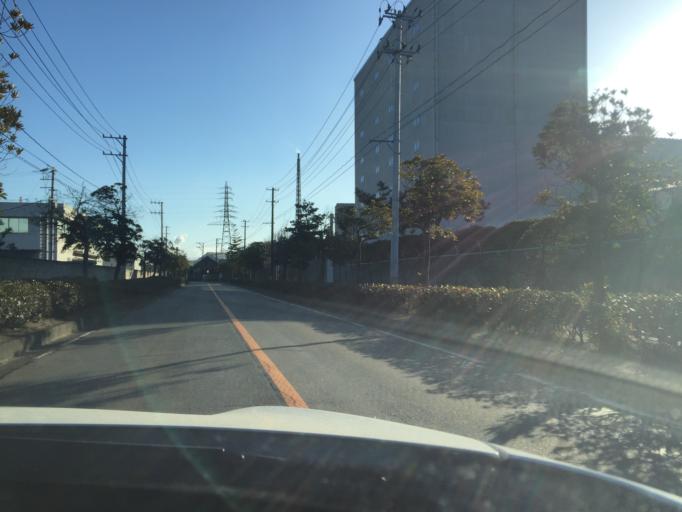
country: JP
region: Fukushima
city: Iwaki
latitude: 36.9389
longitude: 140.8662
